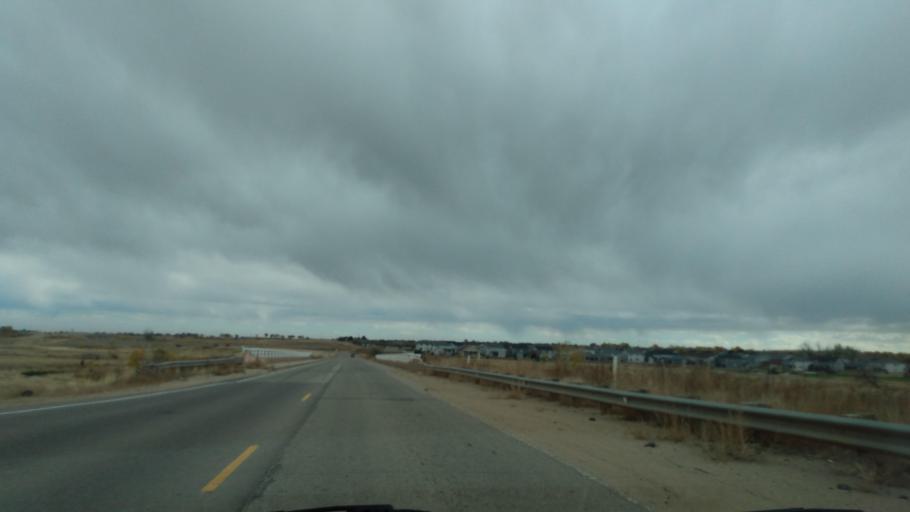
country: US
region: Colorado
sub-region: Adams County
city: Northglenn
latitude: 39.9727
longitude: -104.9670
